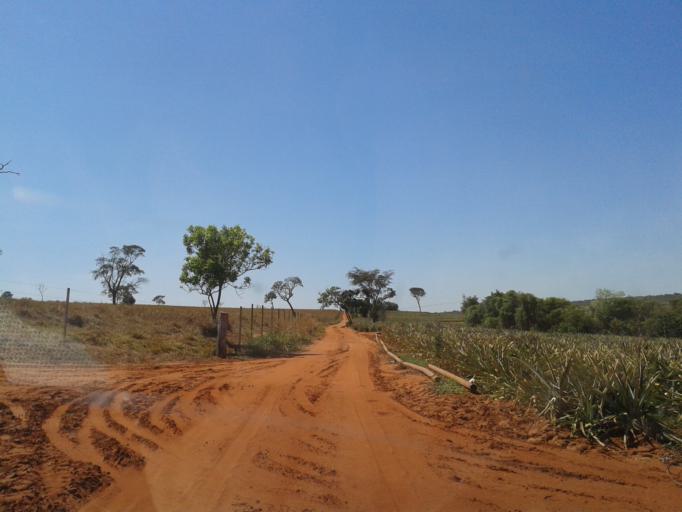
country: BR
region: Minas Gerais
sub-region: Monte Alegre De Minas
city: Monte Alegre de Minas
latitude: -18.8286
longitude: -49.1296
